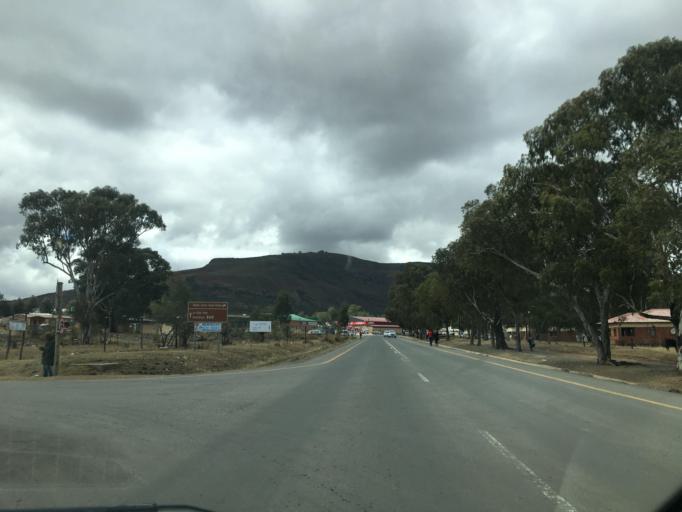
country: ZA
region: Eastern Cape
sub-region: Chris Hani District Municipality
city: Cala
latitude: -31.5272
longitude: 27.6910
